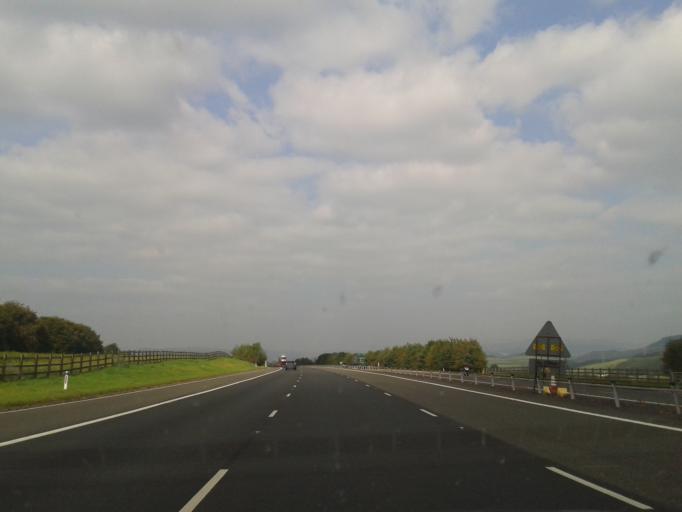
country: GB
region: Scotland
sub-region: Dumfries and Galloway
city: Moffat
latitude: 55.2687
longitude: -3.4182
